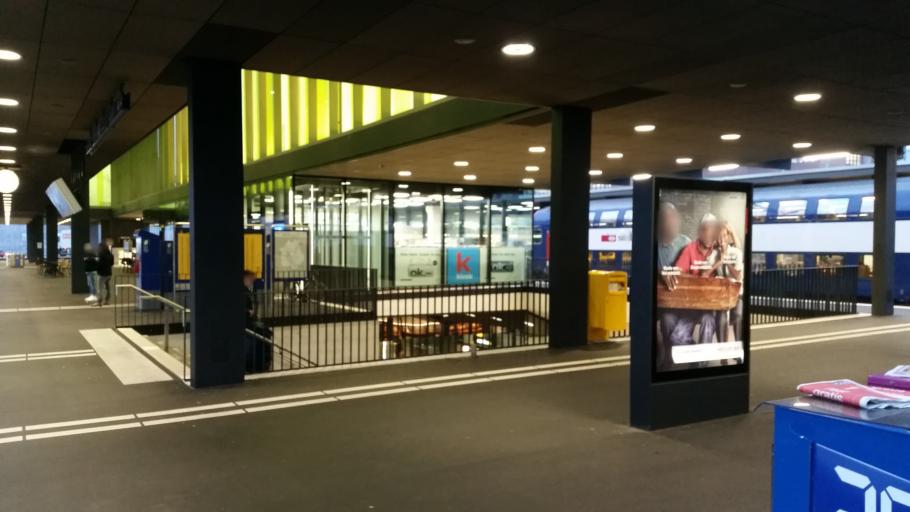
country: CH
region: Zurich
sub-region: Bezirk Zuerich
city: Zuerich (Kreis 11) / Oerlikon
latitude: 47.4111
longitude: 8.5439
